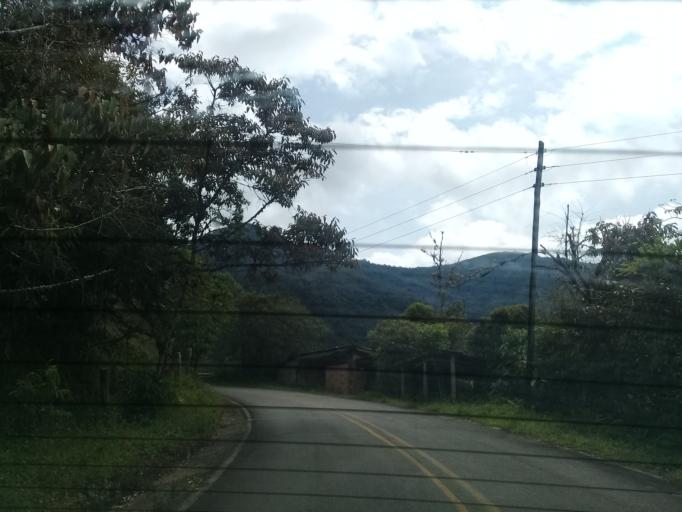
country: CO
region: Cundinamarca
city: Gachala
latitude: 4.7005
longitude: -73.4559
